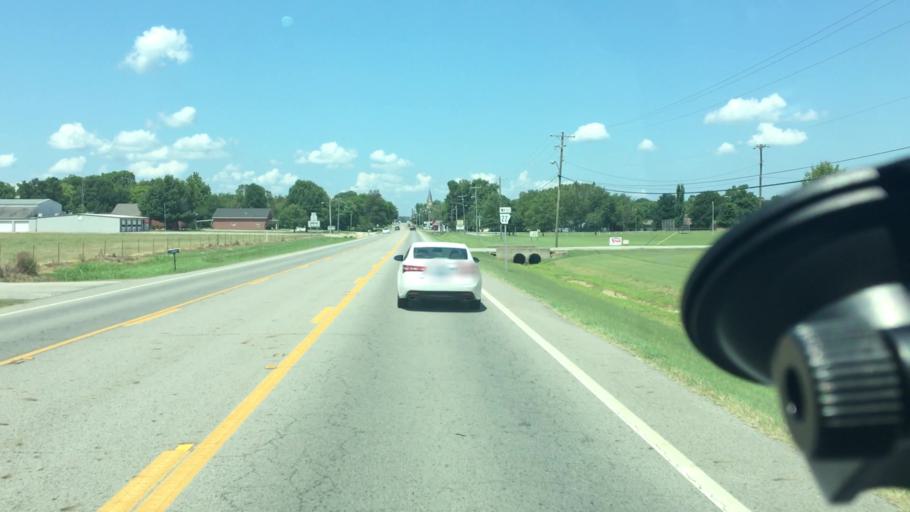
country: US
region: Arkansas
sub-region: Franklin County
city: Charleston
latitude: 35.2970
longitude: -94.0270
